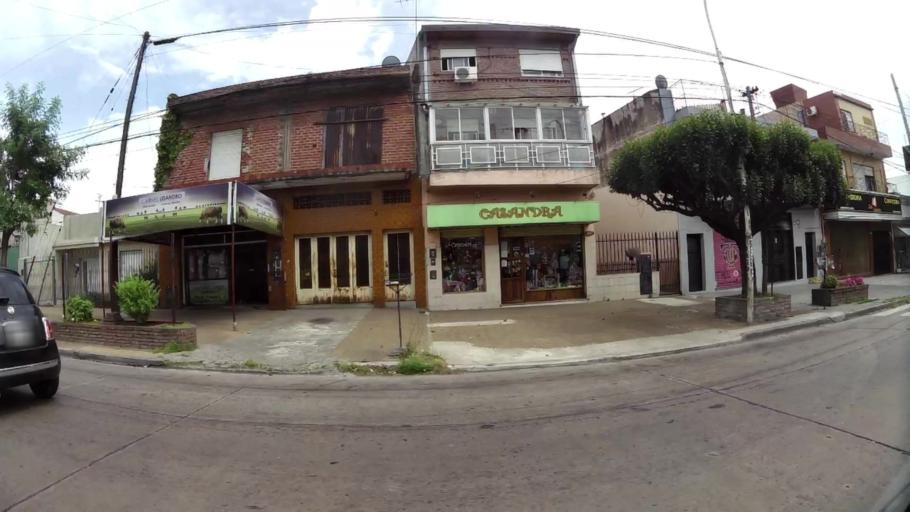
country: AR
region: Buenos Aires F.D.
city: Villa Lugano
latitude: -34.6881
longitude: -58.4958
